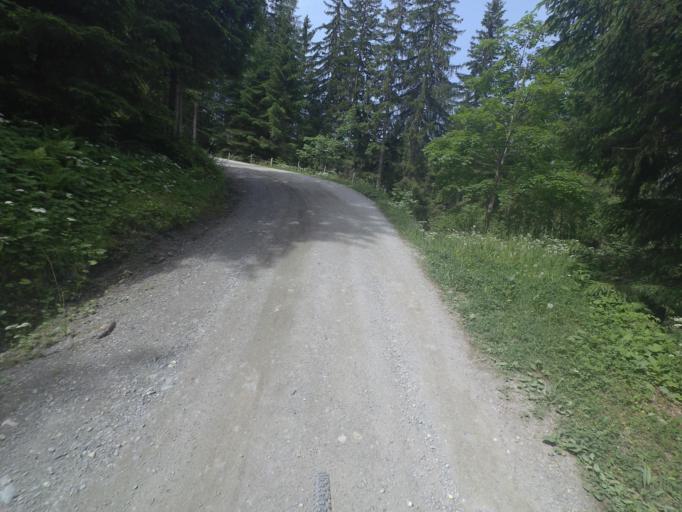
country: AT
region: Salzburg
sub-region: Politischer Bezirk Sankt Johann im Pongau
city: Muhlbach am Hochkonig
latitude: 47.3544
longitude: 13.1179
